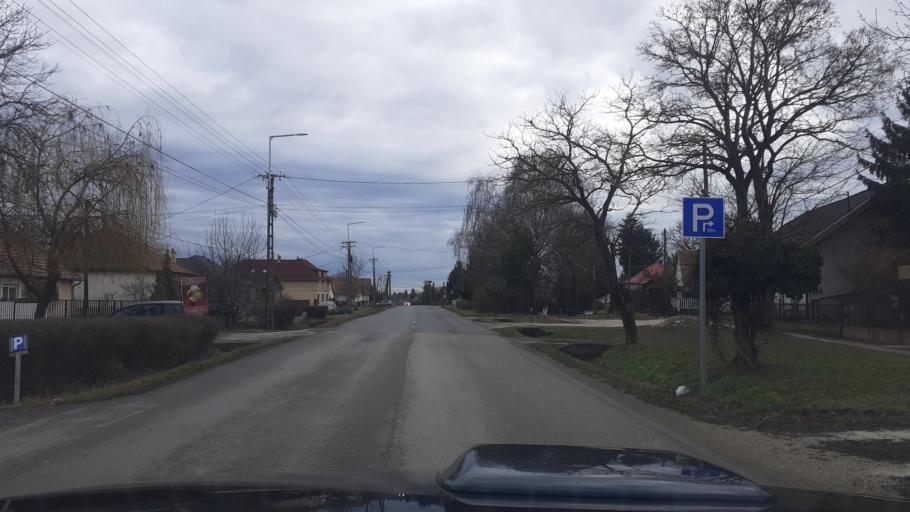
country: HU
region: Fejer
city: Seregelyes
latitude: 47.1154
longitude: 18.5728
